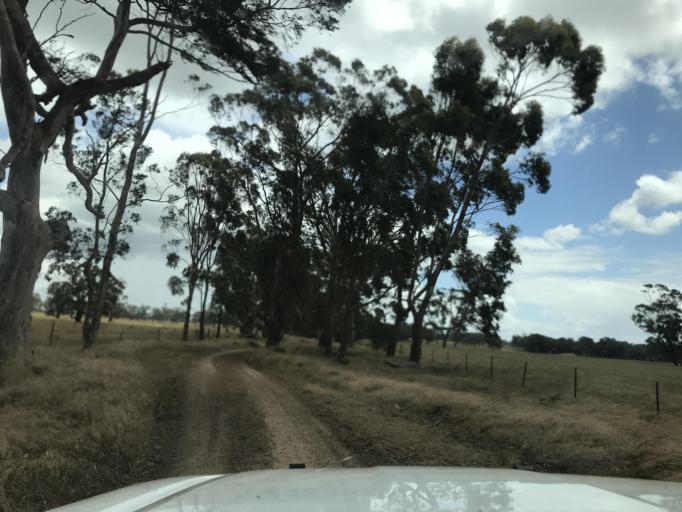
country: AU
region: South Australia
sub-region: Wattle Range
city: Penola
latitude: -37.0887
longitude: 141.3322
